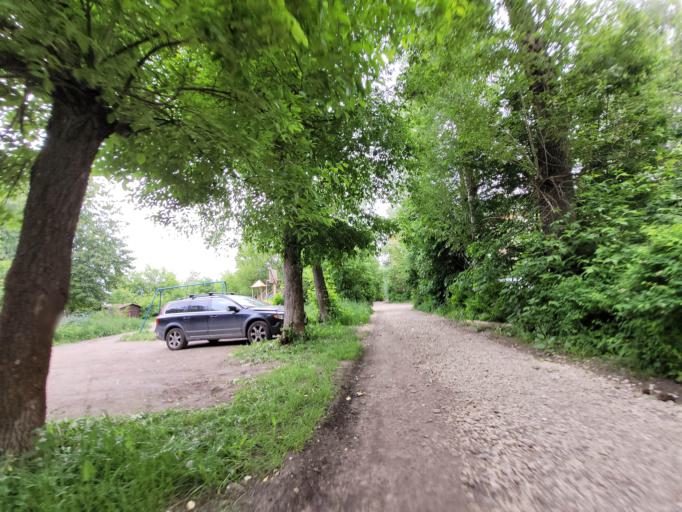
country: RU
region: Moskovskaya
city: Lesnyye Polyany
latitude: 55.9447
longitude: 37.8633
